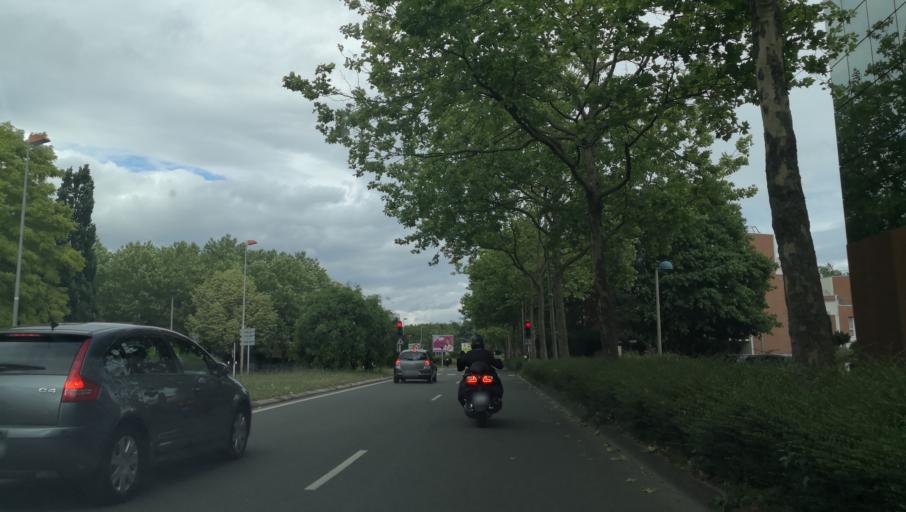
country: FR
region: Ile-de-France
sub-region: Departement des Yvelines
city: Saint-Cyr-l'Ecole
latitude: 48.7853
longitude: 2.0556
